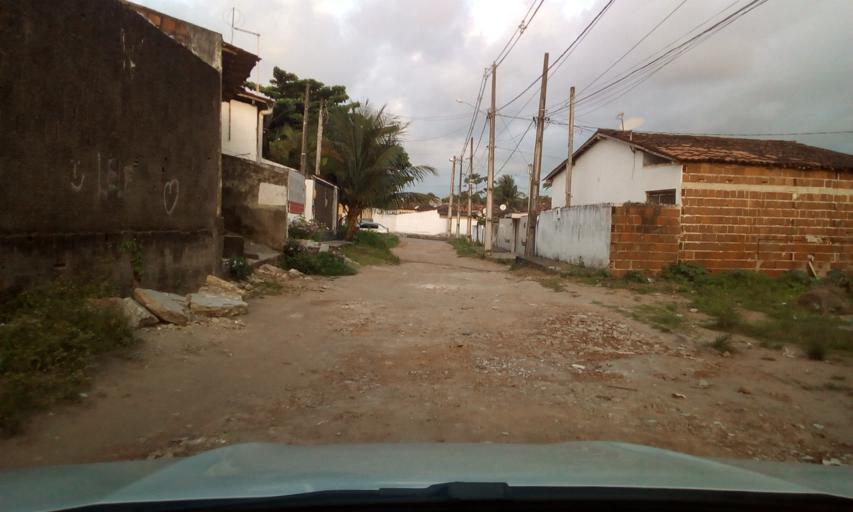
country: BR
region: Paraiba
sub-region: Bayeux
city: Bayeux
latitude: -7.1822
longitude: -34.8920
